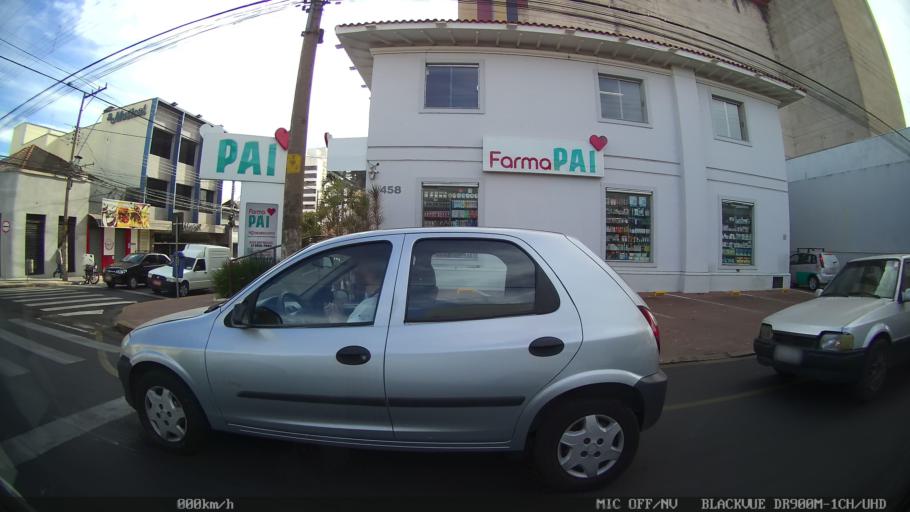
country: BR
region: Sao Paulo
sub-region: Catanduva
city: Catanduva
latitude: -21.1383
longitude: -48.9742
